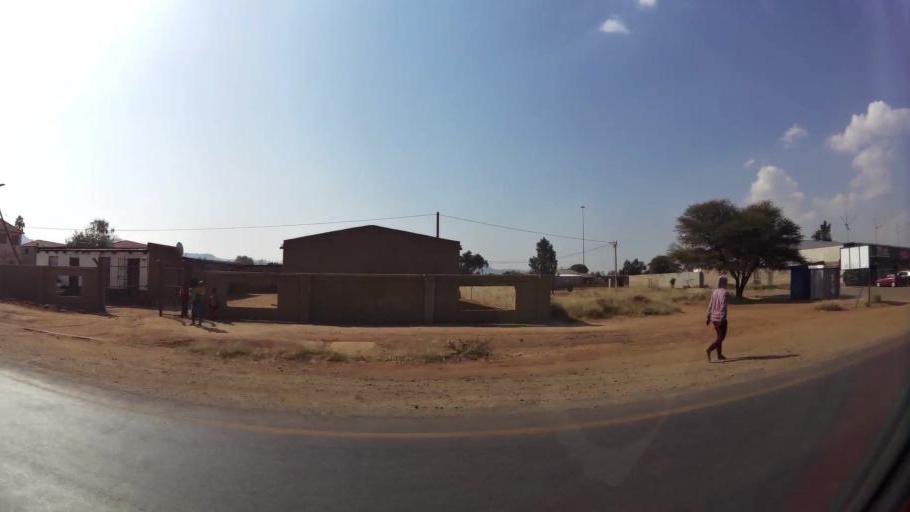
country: ZA
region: North-West
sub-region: Bojanala Platinum District Municipality
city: Mogwase
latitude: -25.3814
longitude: 27.0648
